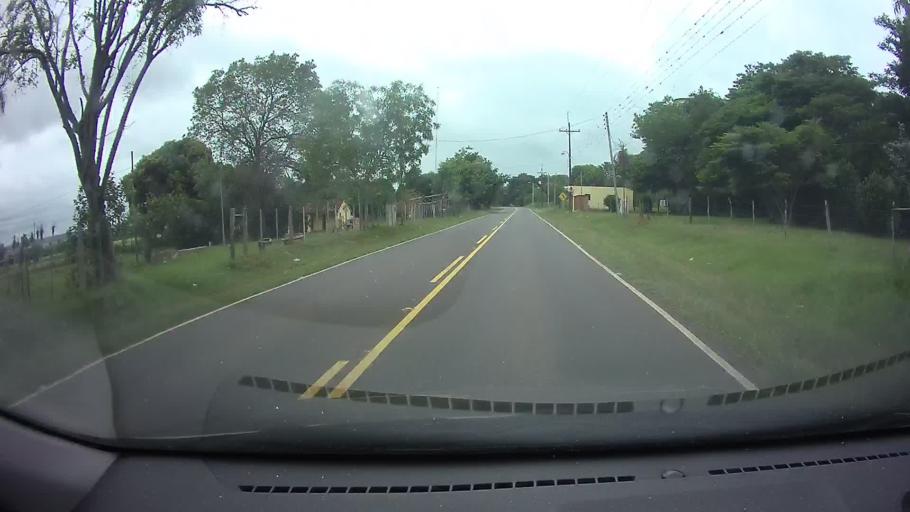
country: PY
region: Central
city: Nueva Italia
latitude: -25.6085
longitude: -57.4247
